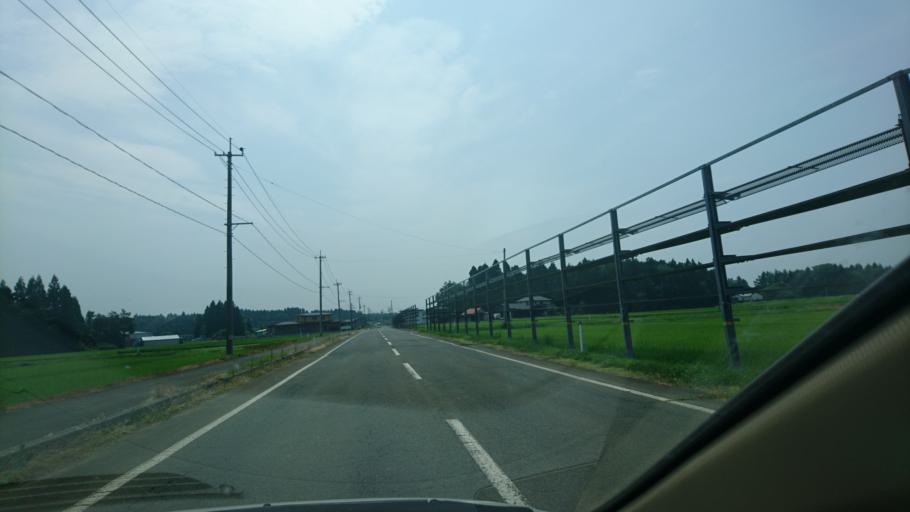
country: JP
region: Iwate
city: Kitakami
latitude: 39.2560
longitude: 141.0824
